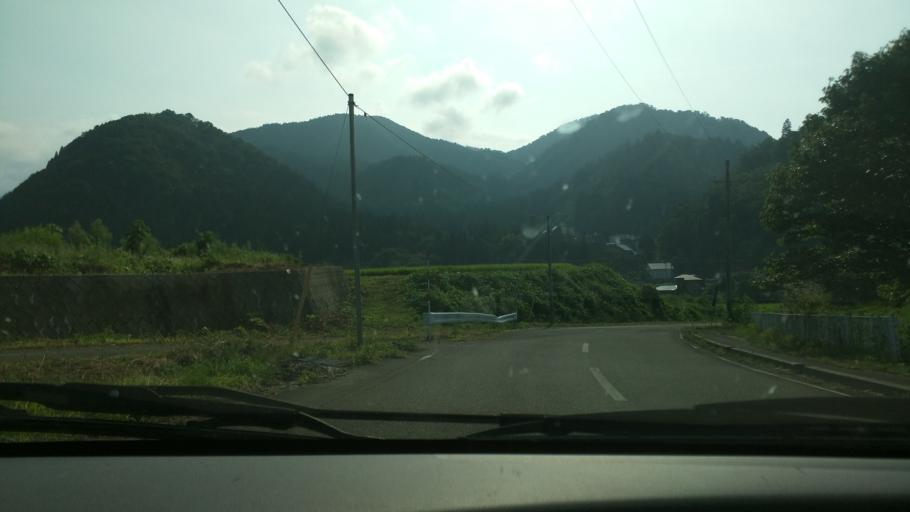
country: JP
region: Fukushima
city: Kitakata
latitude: 37.7320
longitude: 139.8795
